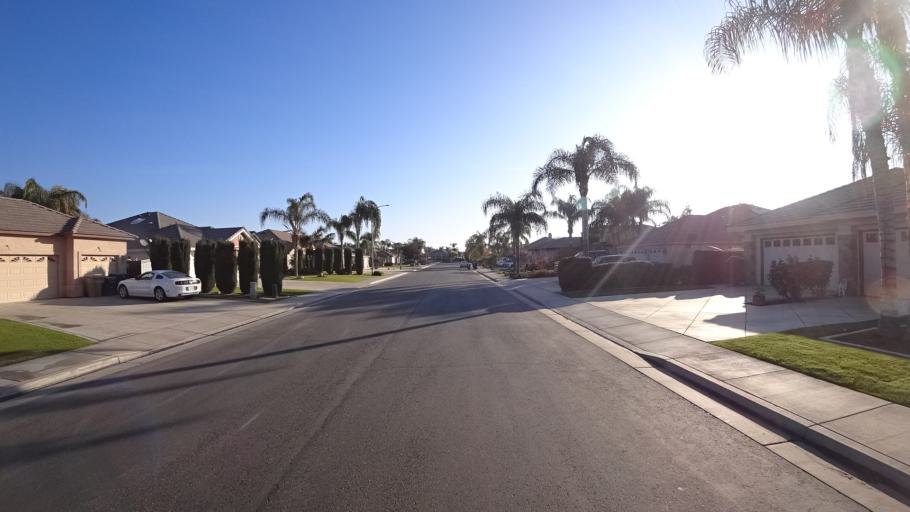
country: US
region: California
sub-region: Kern County
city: Greenfield
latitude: 35.2748
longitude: -119.0523
